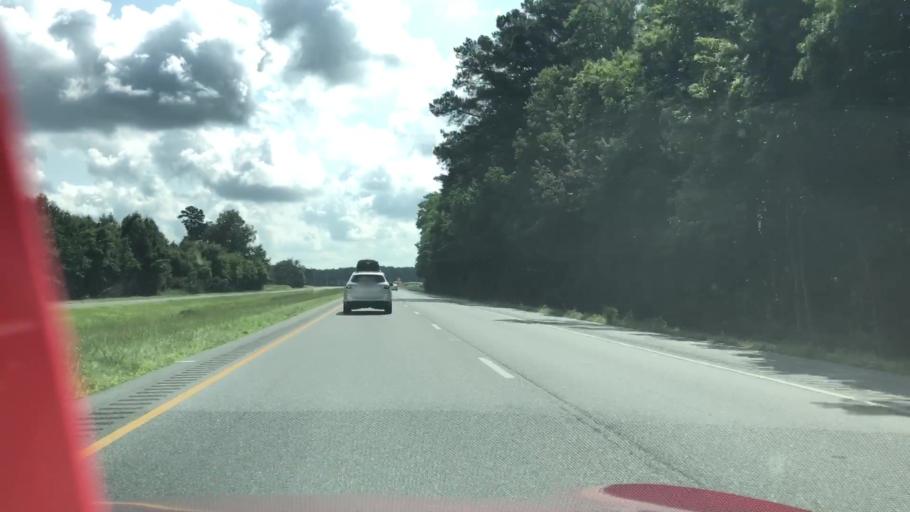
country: US
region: Maryland
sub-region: Somerset County
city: Princess Anne
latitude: 38.1186
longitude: -75.6681
